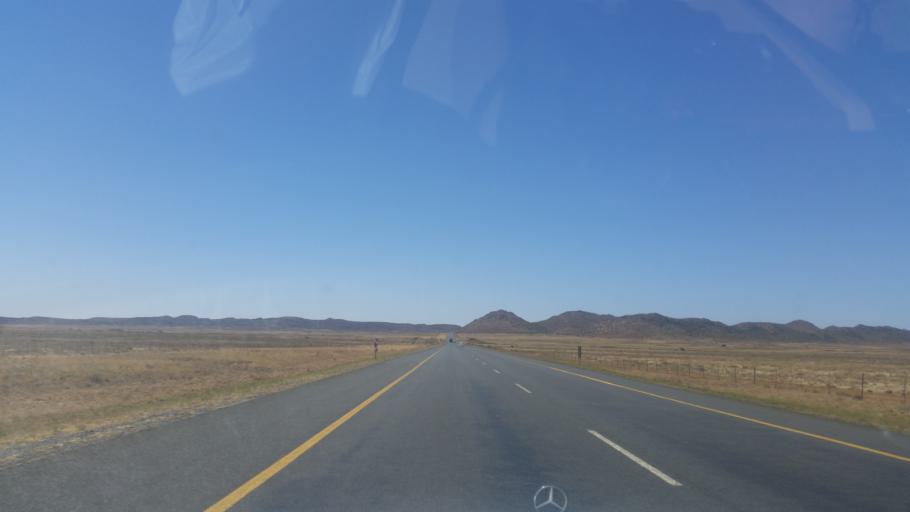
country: ZA
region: Northern Cape
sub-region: Pixley ka Seme District Municipality
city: Colesberg
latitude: -30.6740
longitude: 25.1715
